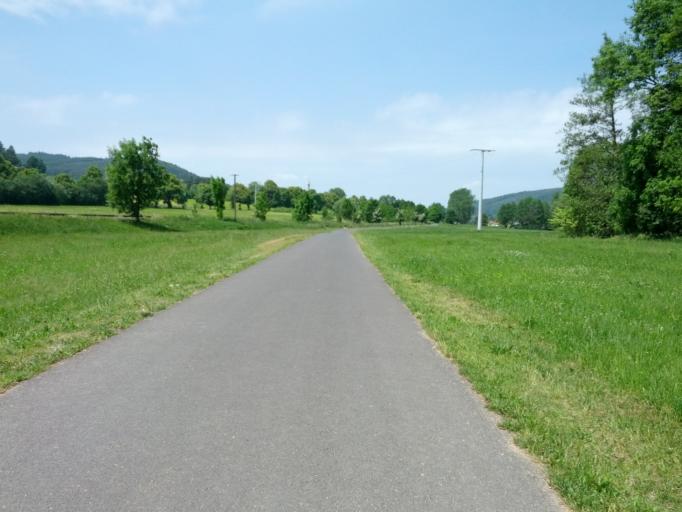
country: DE
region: Thuringia
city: Weilar
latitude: 50.7708
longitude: 10.1403
